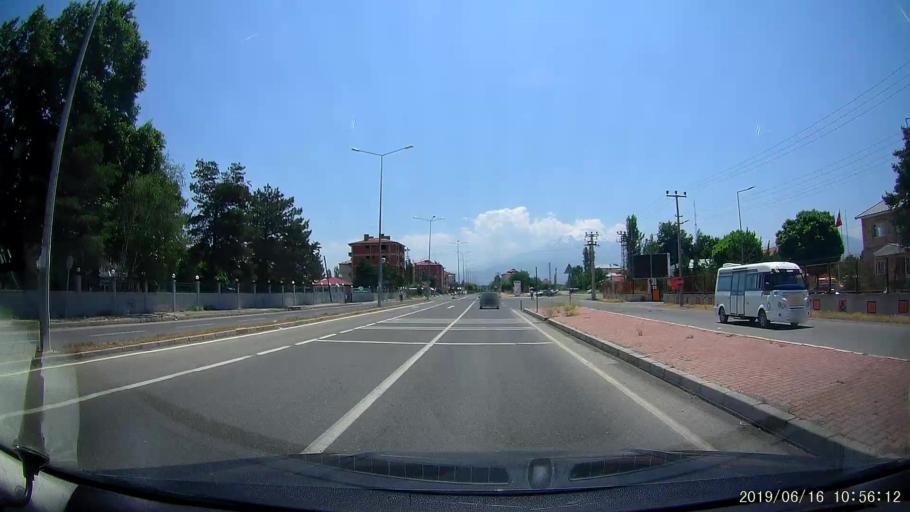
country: TR
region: Igdir
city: Igdir
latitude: 39.9313
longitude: 44.0195
